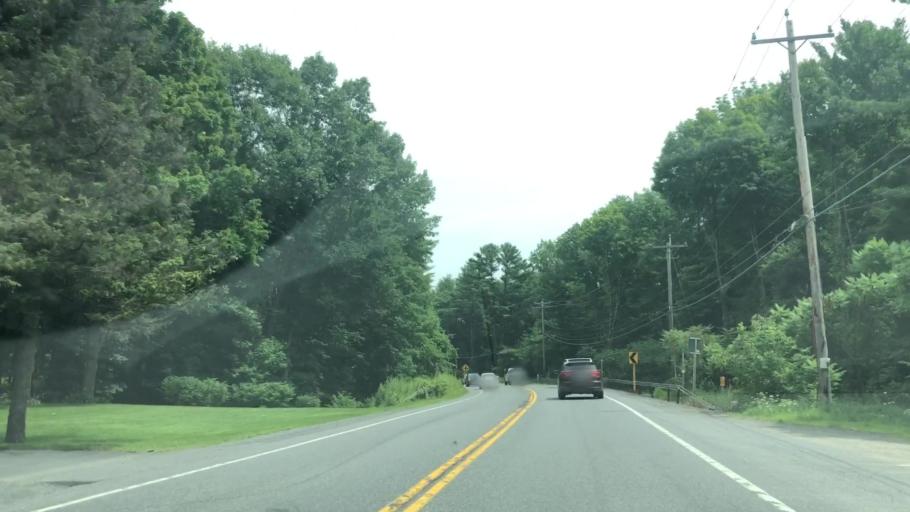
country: US
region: New York
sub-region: Warren County
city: Queensbury
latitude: 43.4028
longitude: -73.5866
